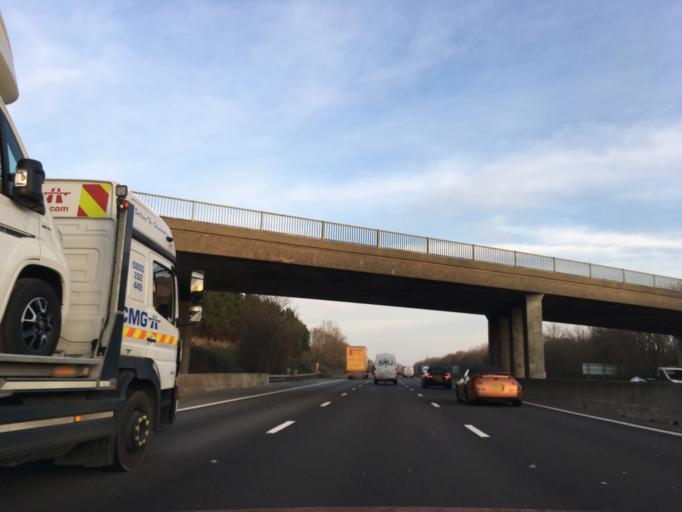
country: GB
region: England
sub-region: Worcestershire
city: Bredon
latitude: 52.0030
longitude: -2.1226
